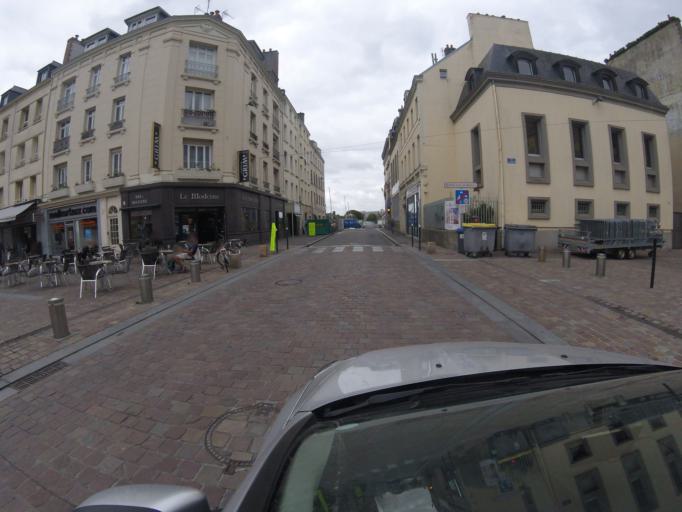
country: FR
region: Lower Normandy
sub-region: Departement de la Manche
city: Cherbourg-Octeville
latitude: 49.6380
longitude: -1.6225
